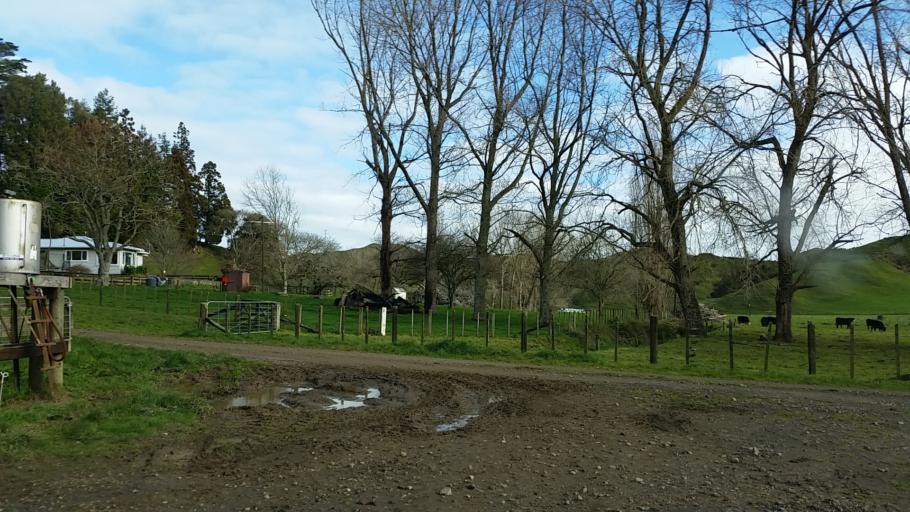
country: NZ
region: Taranaki
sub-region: South Taranaki District
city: Eltham
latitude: -39.2517
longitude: 174.5424
